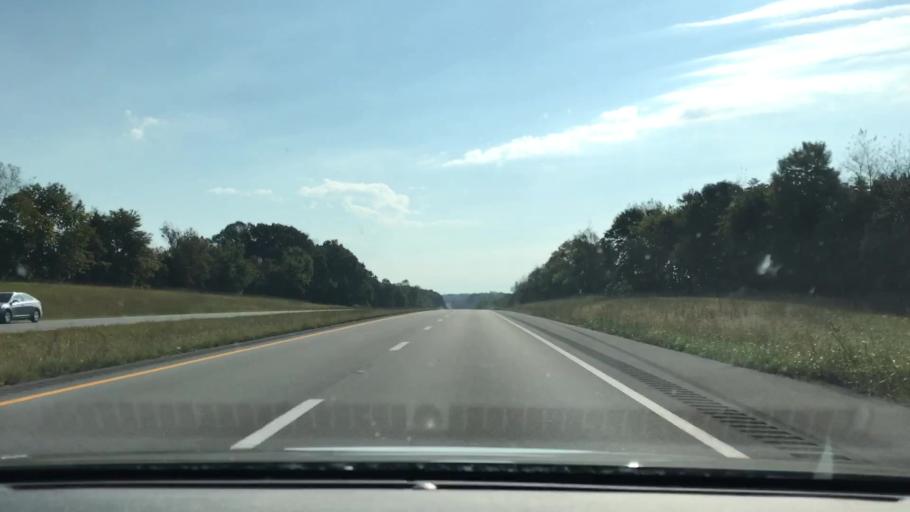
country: US
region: Kentucky
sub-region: Adair County
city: Columbia
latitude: 37.0691
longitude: -85.2097
